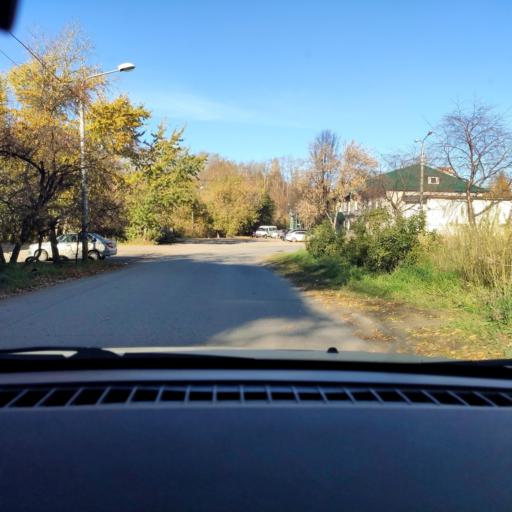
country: RU
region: Perm
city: Perm
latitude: 58.1137
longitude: 56.3734
